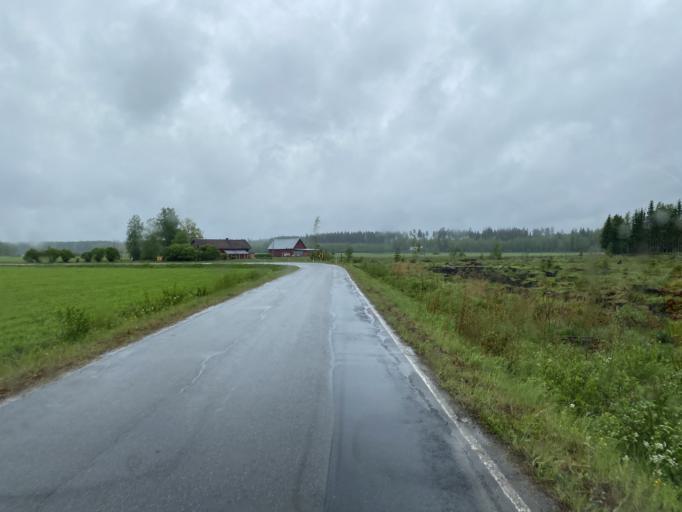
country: FI
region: Haeme
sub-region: Forssa
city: Humppila
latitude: 61.0560
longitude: 23.3260
